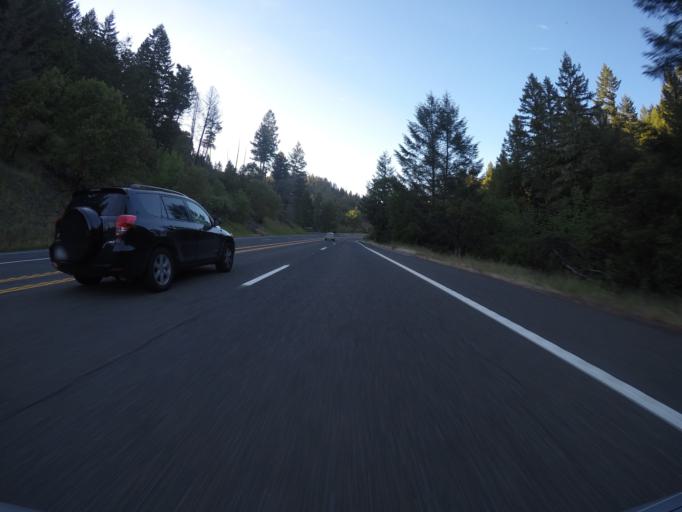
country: US
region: California
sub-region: Mendocino County
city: Laytonville
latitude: 39.5974
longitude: -123.4543
